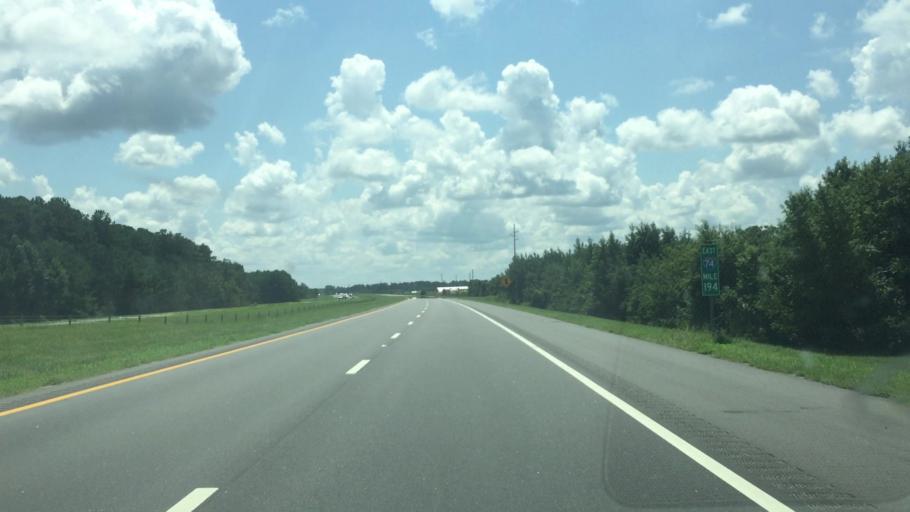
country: US
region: North Carolina
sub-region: Robeson County
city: Maxton
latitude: 34.7147
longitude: -79.3106
